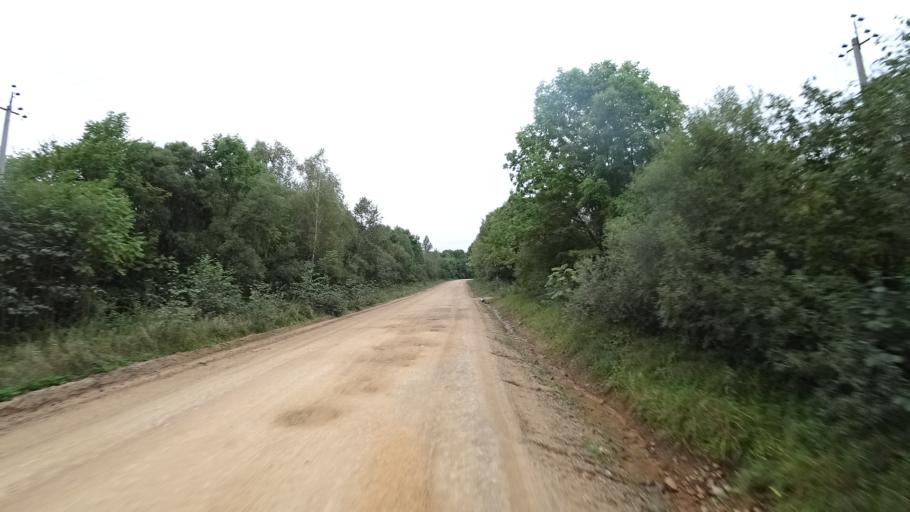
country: RU
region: Primorskiy
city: Rettikhovka
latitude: 44.1814
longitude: 132.8046
